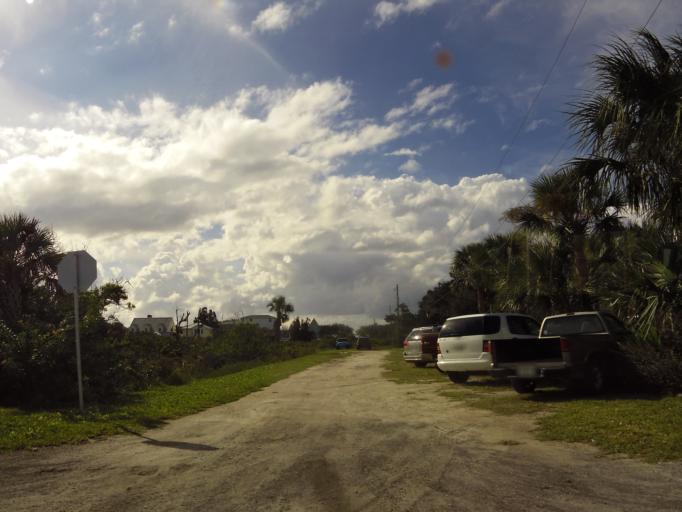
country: US
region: Florida
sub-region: Saint Johns County
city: Villano Beach
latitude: 29.9218
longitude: -81.2951
